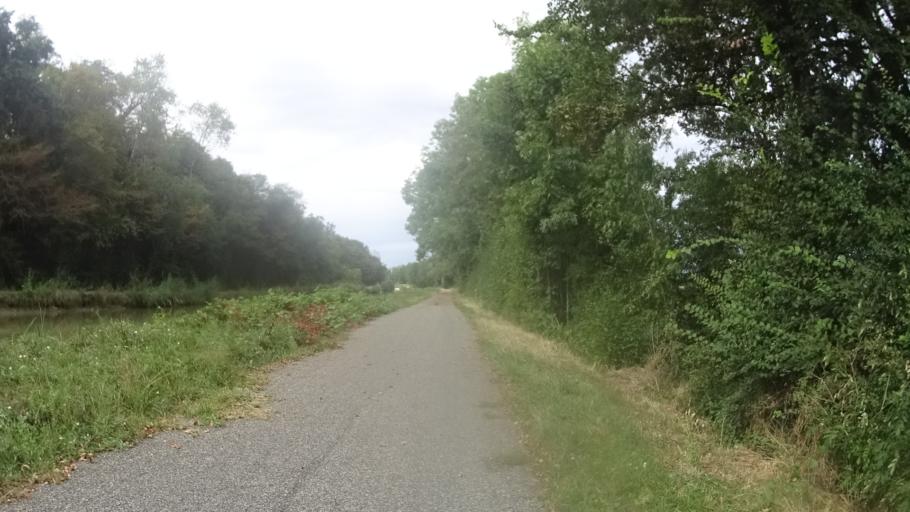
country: FR
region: Bourgogne
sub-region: Departement de la Nievre
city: Sermoise-sur-Loire
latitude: 46.9553
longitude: 3.1994
